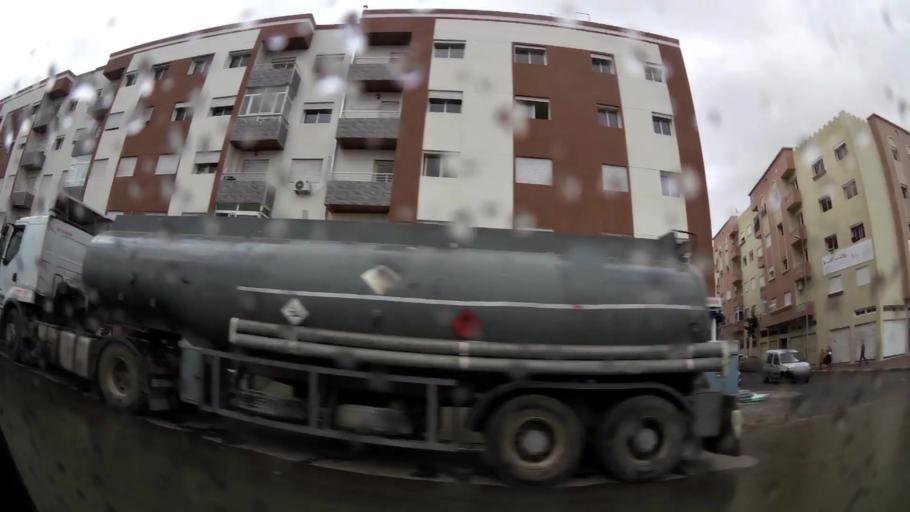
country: MA
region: Grand Casablanca
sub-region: Mohammedia
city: Mohammedia
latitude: 33.6801
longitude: -7.4030
